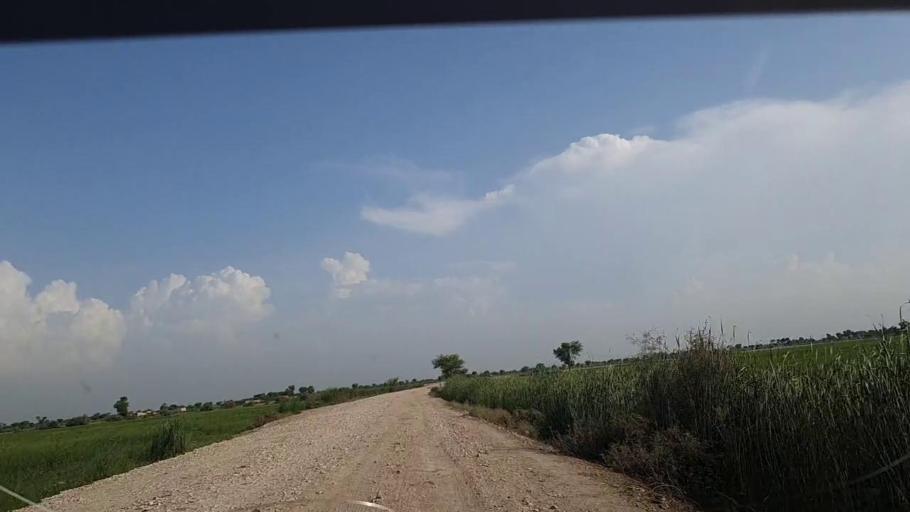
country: PK
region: Sindh
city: Khanpur
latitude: 27.8531
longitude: 69.3772
